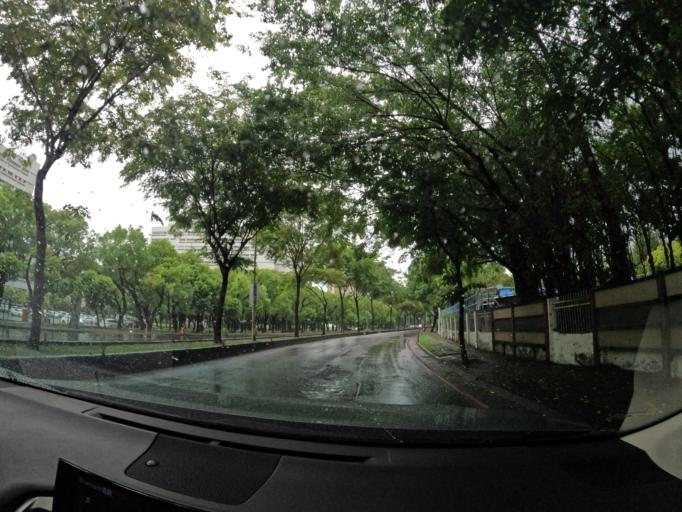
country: TW
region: Taiwan
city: Fengshan
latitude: 22.6509
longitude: 120.3556
